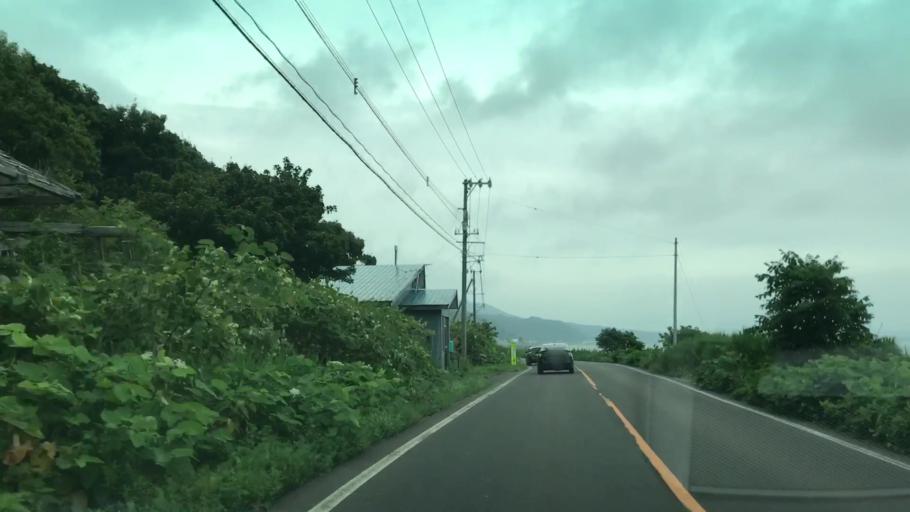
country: JP
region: Hokkaido
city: Iwanai
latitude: 42.8028
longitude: 140.3070
